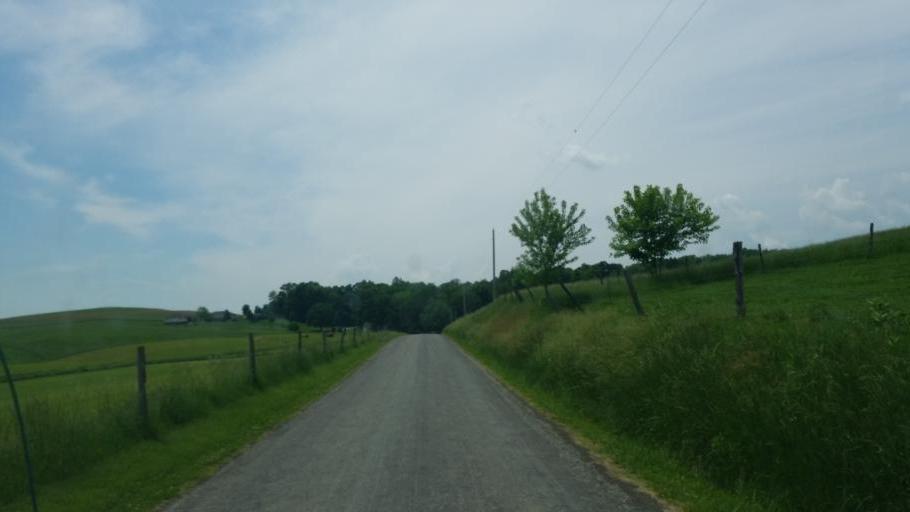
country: US
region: Ohio
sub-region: Tuscarawas County
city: Sugarcreek
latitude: 40.4761
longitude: -81.7693
